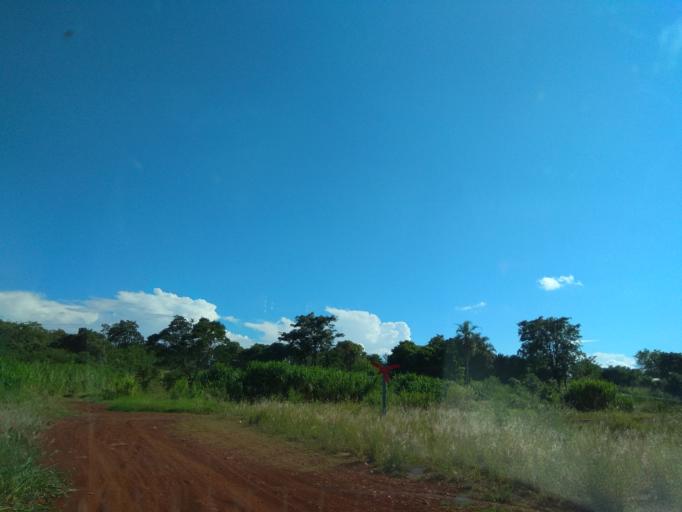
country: AR
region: Misiones
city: Garupa
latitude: -27.4531
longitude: -55.8310
